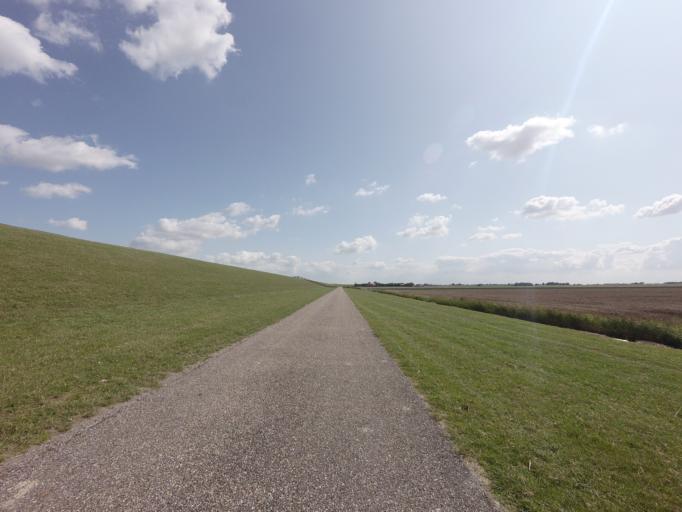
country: NL
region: Friesland
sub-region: Gemeente Ferwerderadiel
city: Hallum
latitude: 53.3247
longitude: 5.7290
